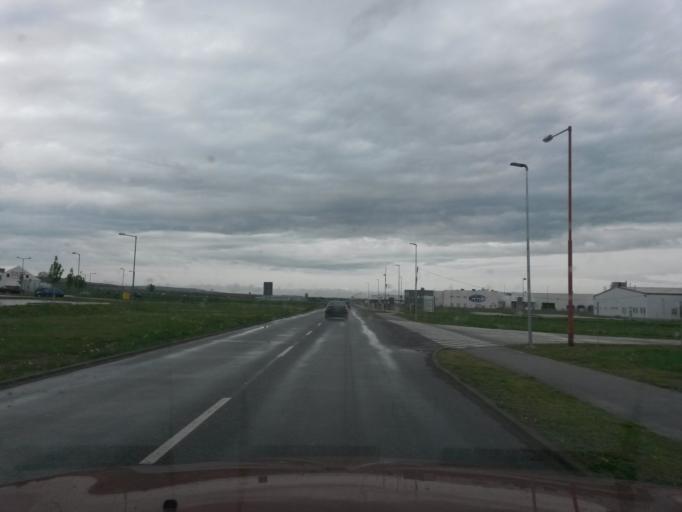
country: HU
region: Borsod-Abauj-Zemplen
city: Gonc
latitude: 48.5508
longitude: 21.2480
